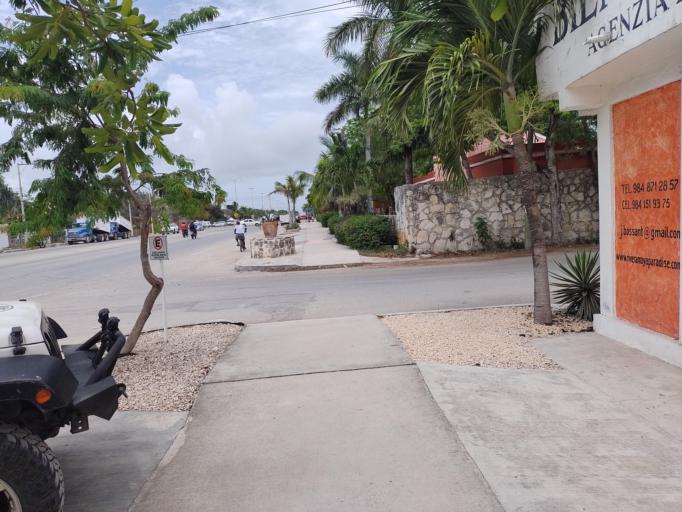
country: MX
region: Quintana Roo
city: Tulum
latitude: 20.2076
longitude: -87.4734
